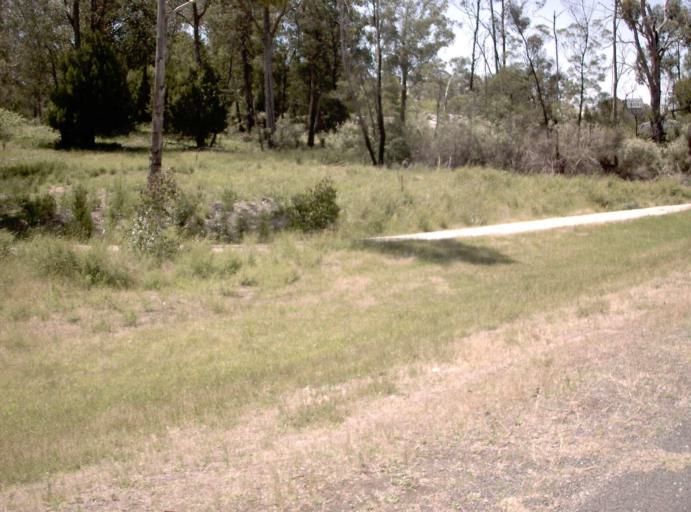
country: AU
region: Victoria
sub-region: East Gippsland
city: Lakes Entrance
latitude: -37.7342
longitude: 148.0860
